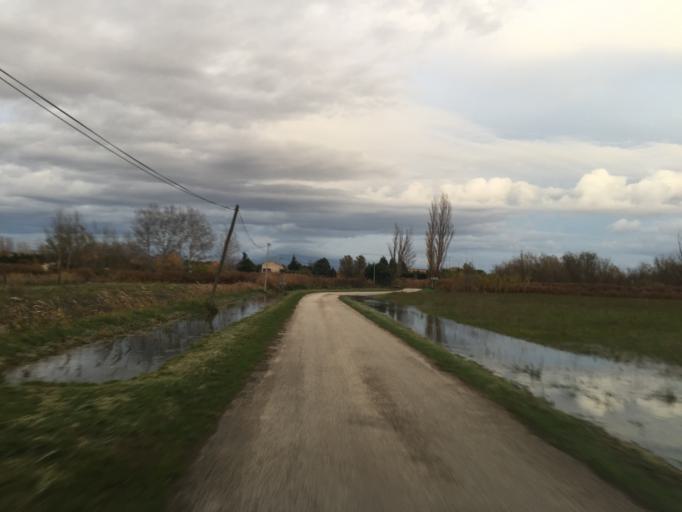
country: FR
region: Provence-Alpes-Cote d'Azur
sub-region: Departement du Vaucluse
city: Courthezon
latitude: 44.0866
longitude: 4.8669
